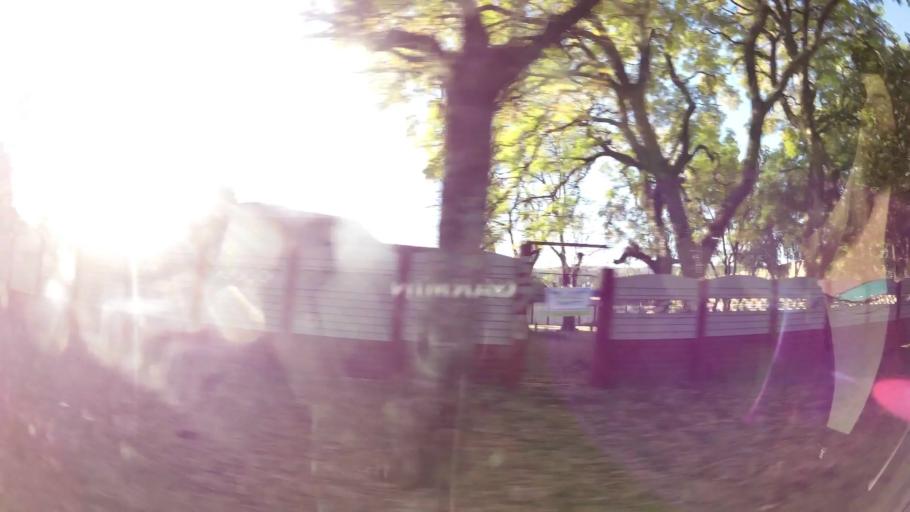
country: ZA
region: Gauteng
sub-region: City of Tshwane Metropolitan Municipality
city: Pretoria
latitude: -25.7047
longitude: 28.2043
